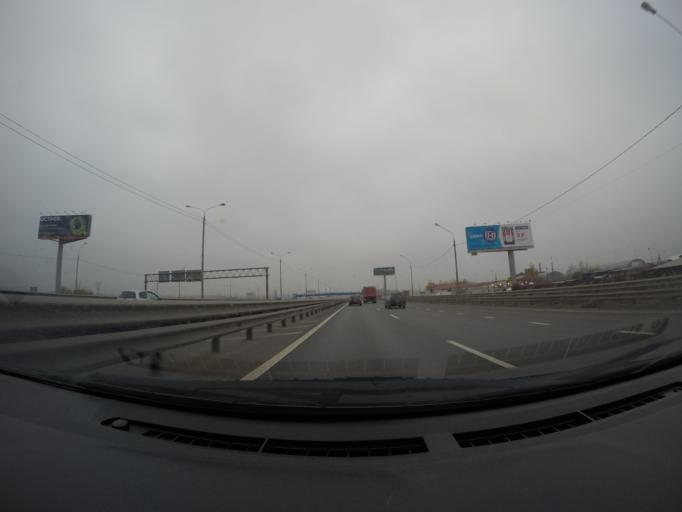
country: RU
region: Moskovskaya
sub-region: Podol'skiy Rayon
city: Podol'sk
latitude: 55.4458
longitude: 37.6174
